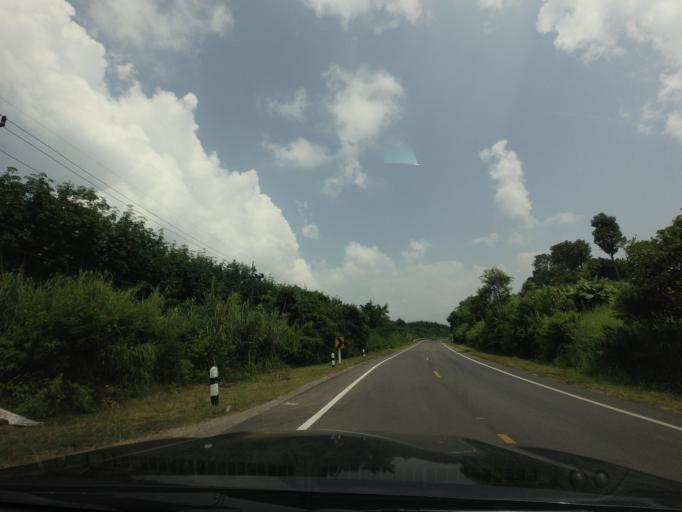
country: TH
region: Nan
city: Santi Suk
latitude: 18.9241
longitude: 100.8937
